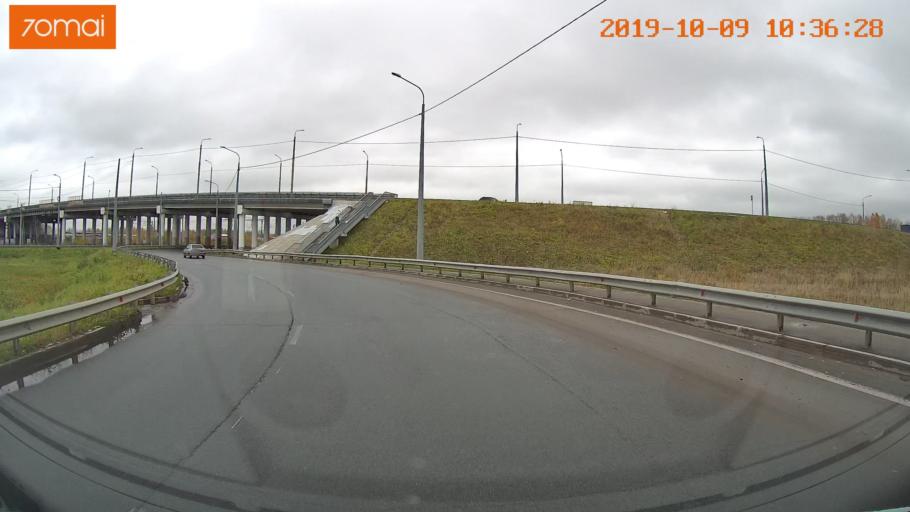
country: RU
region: Vologda
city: Vologda
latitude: 59.2333
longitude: 39.8666
